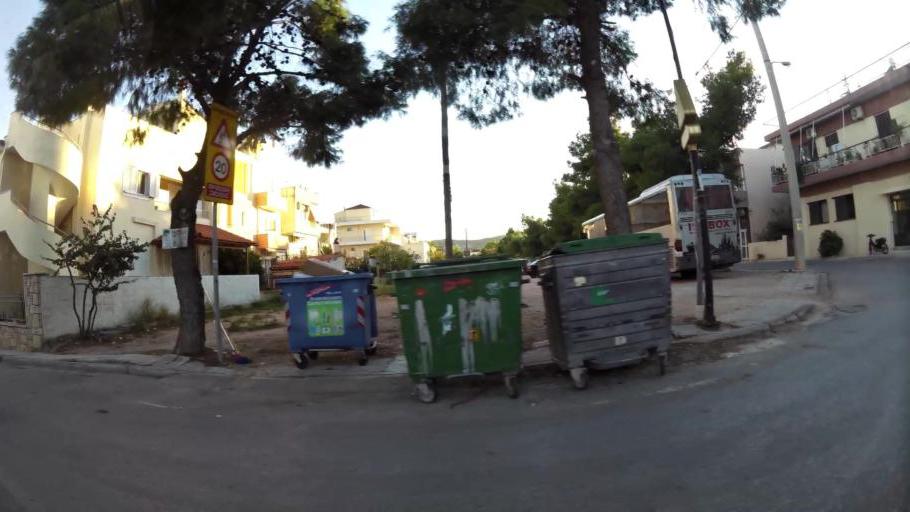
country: GR
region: Attica
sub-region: Nomarchia Dytikis Attikis
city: Ano Liosia
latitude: 38.0835
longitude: 23.7046
